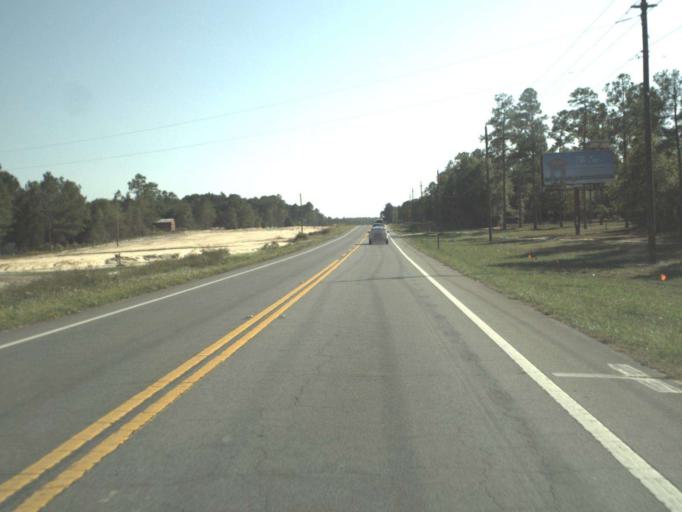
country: US
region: Florida
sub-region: Walton County
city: DeFuniak Springs
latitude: 30.6431
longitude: -86.1146
